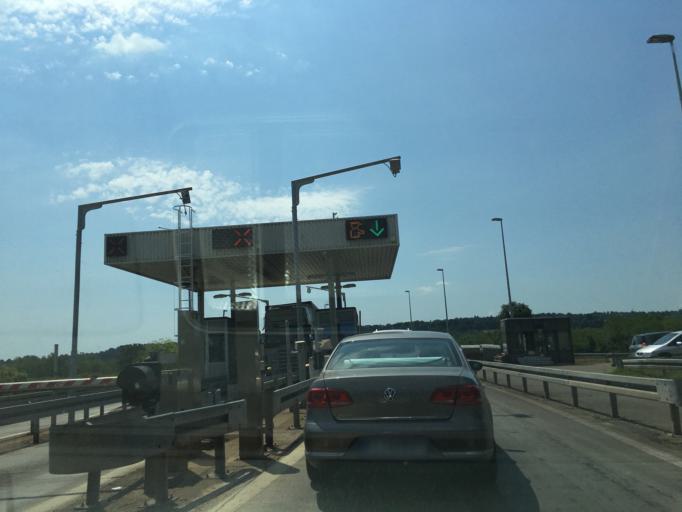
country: RS
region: Central Serbia
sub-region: Podunavski Okrug
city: Smederevo
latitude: 44.5902
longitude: 20.9572
